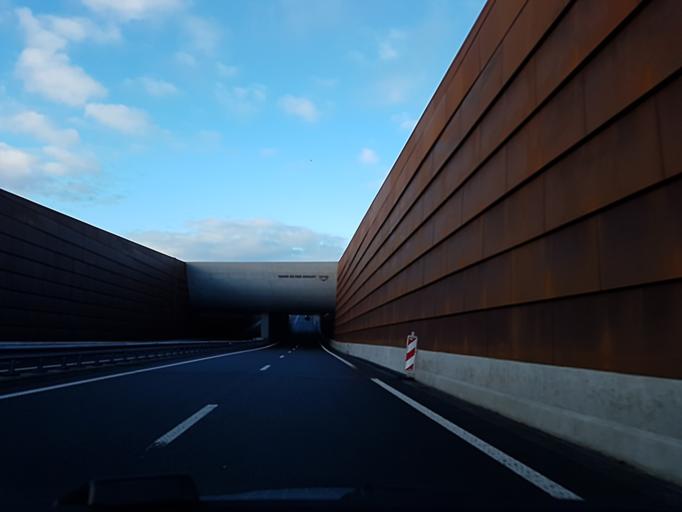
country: NL
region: Friesland
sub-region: Gemeente Tytsjerksteradiel
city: Burgum
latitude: 53.1841
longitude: 5.9826
